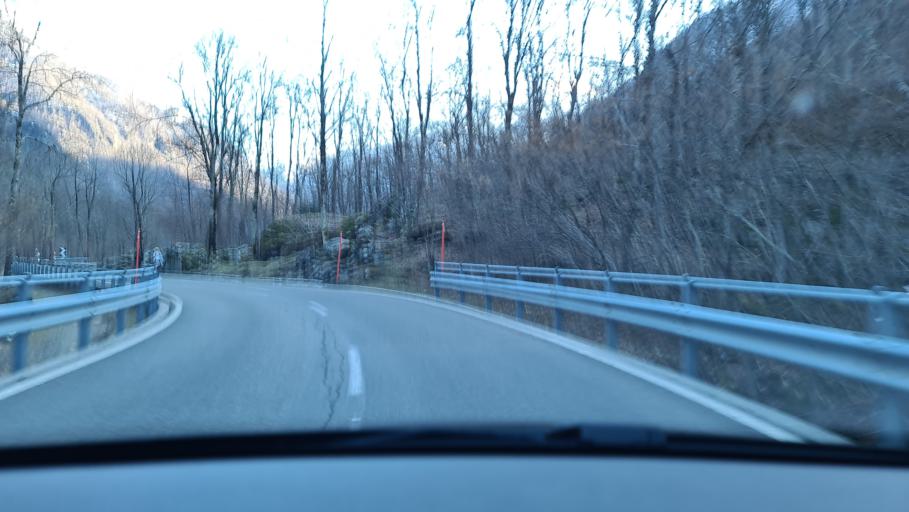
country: CH
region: Ticino
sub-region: Locarno District
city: Lavertezzo
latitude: 46.3315
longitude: 8.8038
